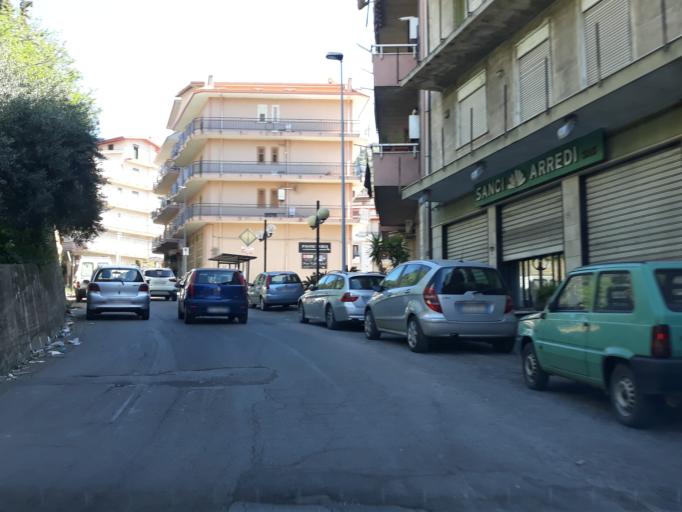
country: IT
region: Sicily
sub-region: Palermo
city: Belmonte Mezzagno
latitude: 38.0459
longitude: 13.3963
